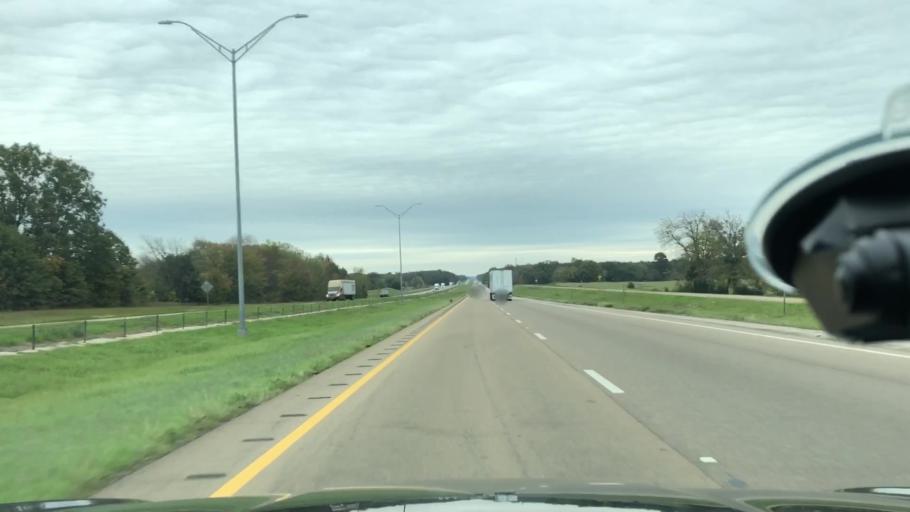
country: US
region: Texas
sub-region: Morris County
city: Omaha
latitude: 33.2462
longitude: -94.8569
